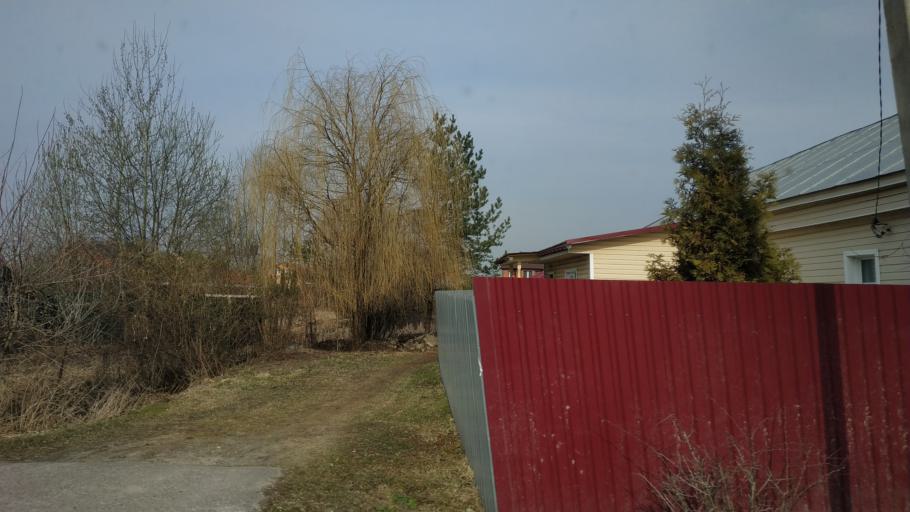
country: RU
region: Moskovskaya
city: Beloozerskiy
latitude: 55.4390
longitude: 38.4892
